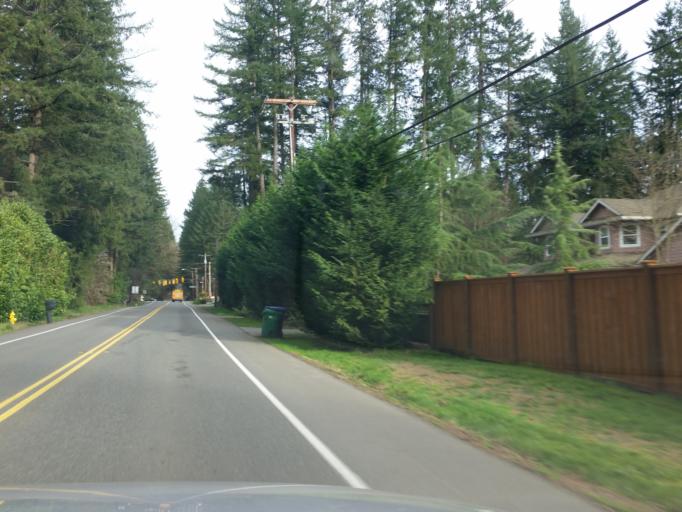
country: US
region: Washington
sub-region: King County
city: Cottage Lake
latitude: 47.7474
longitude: -122.0850
